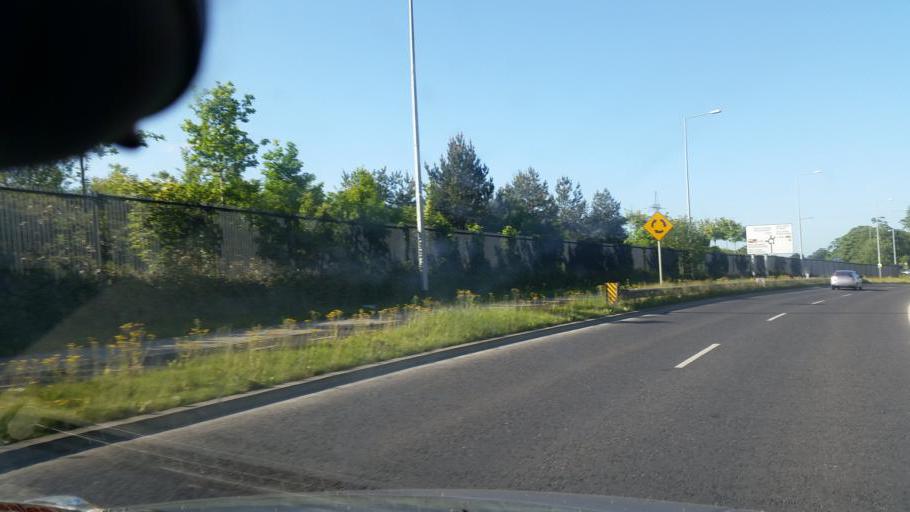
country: IE
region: Leinster
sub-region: Fingal County
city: Blanchardstown
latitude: 53.4150
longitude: -6.3851
